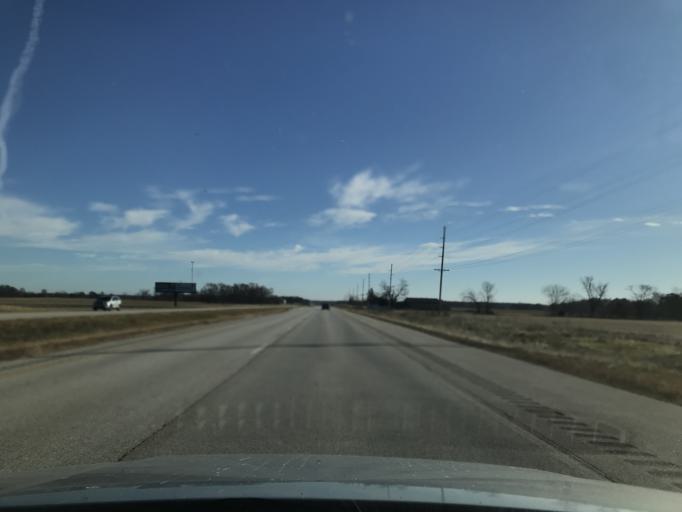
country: US
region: Illinois
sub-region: Hancock County
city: Carthage
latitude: 40.4148
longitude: -91.0471
